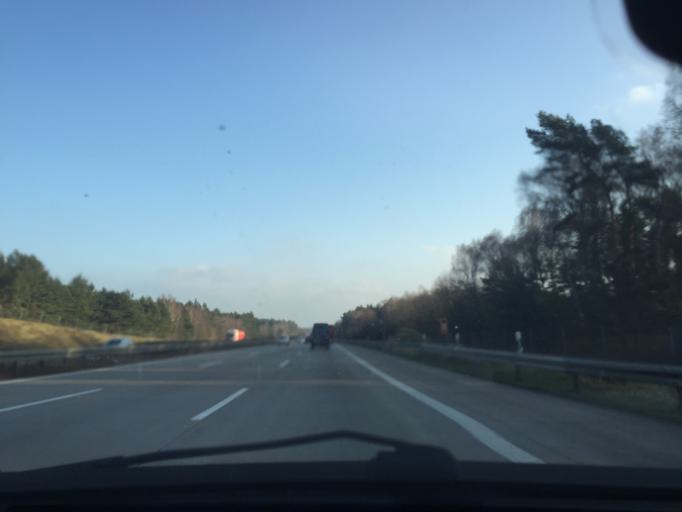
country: DE
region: Saxony-Anhalt
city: Moser
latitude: 52.2285
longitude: 11.7784
